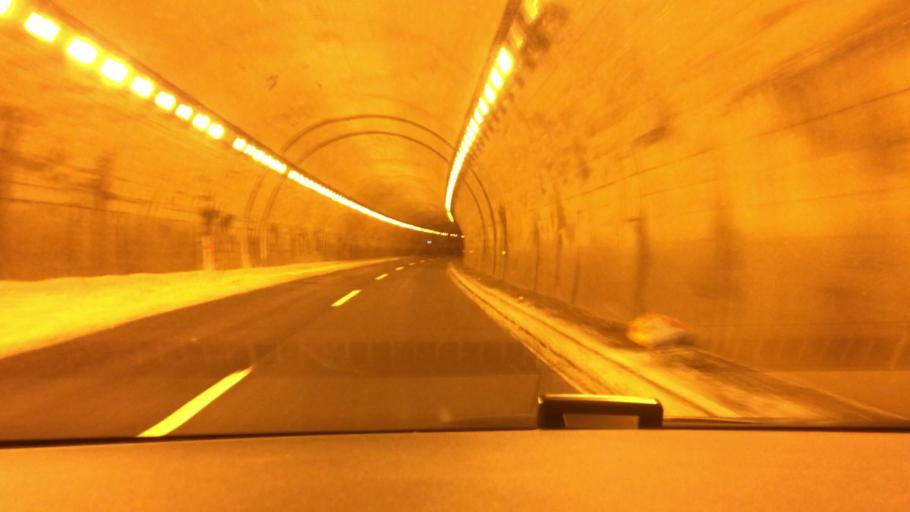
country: JP
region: Akita
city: Hanawa
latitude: 40.1150
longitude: 140.8653
